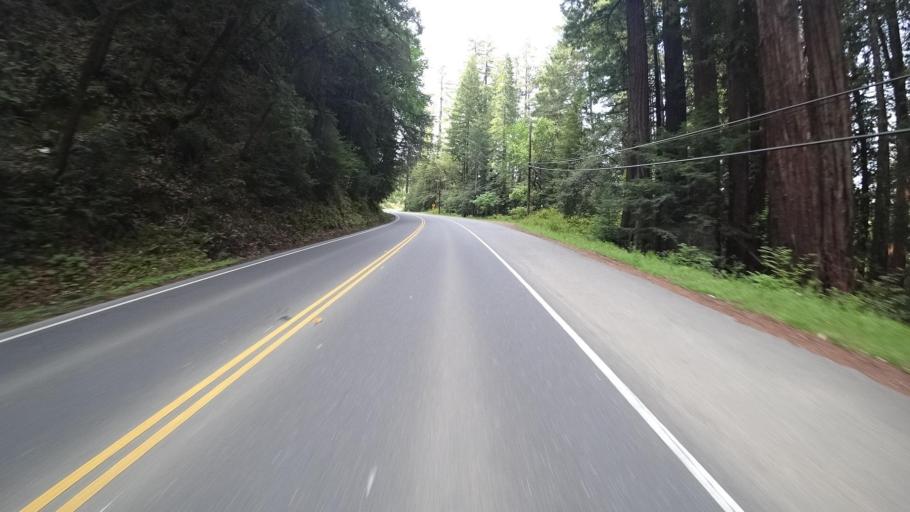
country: US
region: California
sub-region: Humboldt County
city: Redway
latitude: 40.1309
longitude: -123.8182
